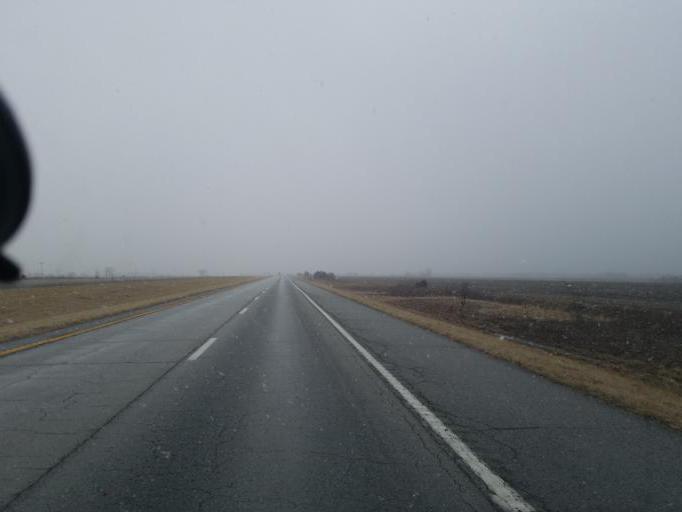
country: US
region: Missouri
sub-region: Macon County
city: La Plata
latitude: 39.9451
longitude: -92.4772
